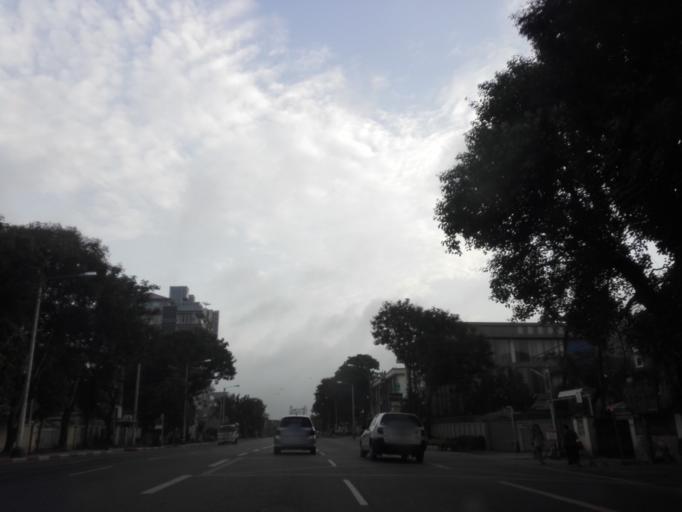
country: MM
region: Yangon
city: Yangon
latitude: 16.8556
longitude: 96.1412
